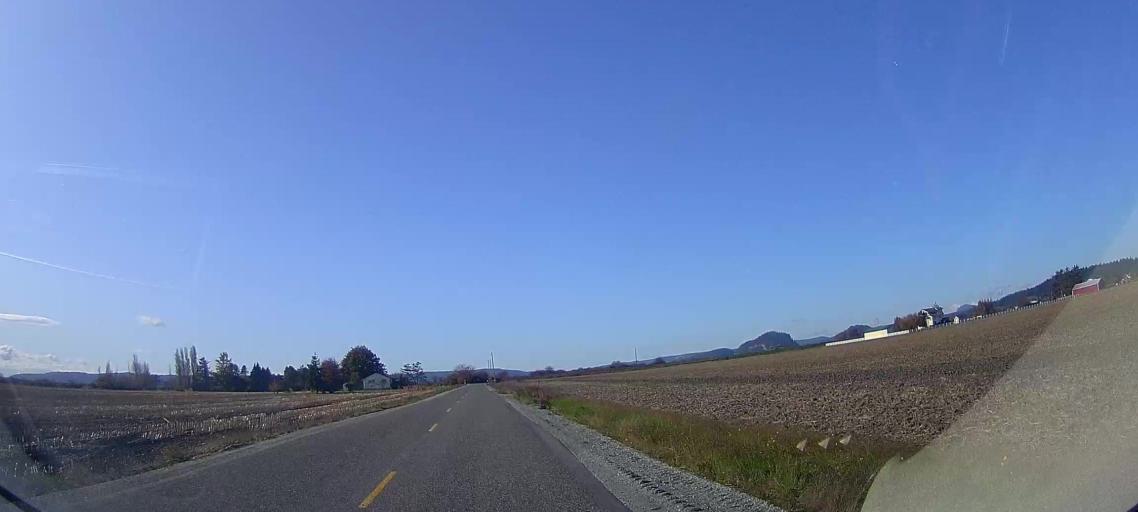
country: US
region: Washington
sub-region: Snohomish County
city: Stanwood
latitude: 48.3411
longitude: -122.4346
